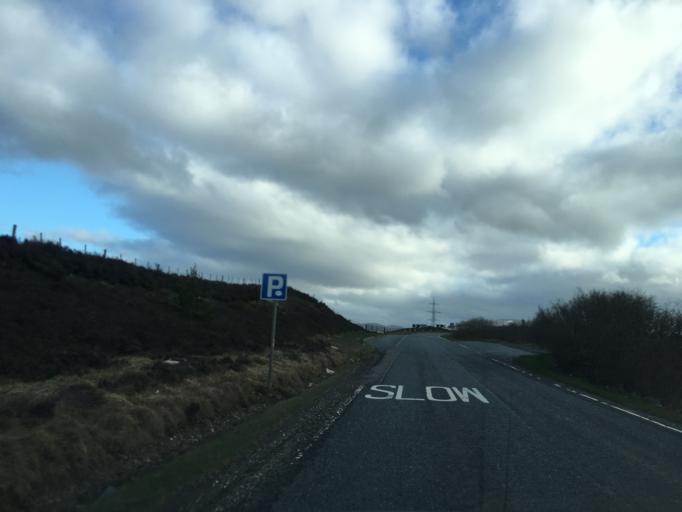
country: GB
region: Scotland
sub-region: Highland
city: Kingussie
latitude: 56.9664
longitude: -4.2398
